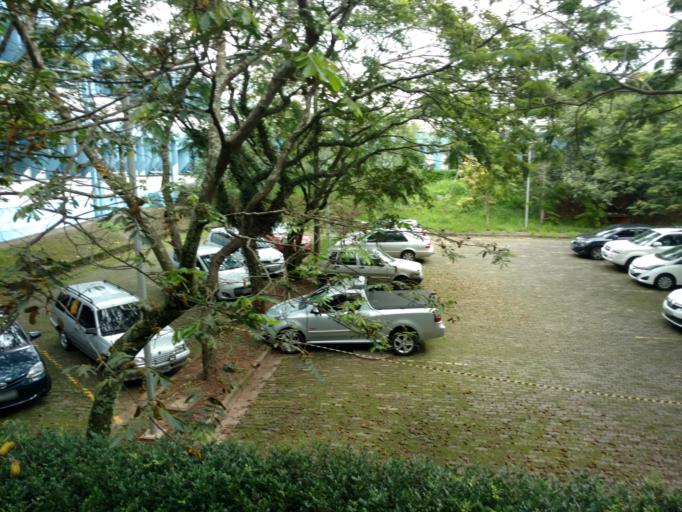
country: BR
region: Sao Paulo
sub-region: Osasco
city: Osasco
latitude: -23.5586
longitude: -46.7320
